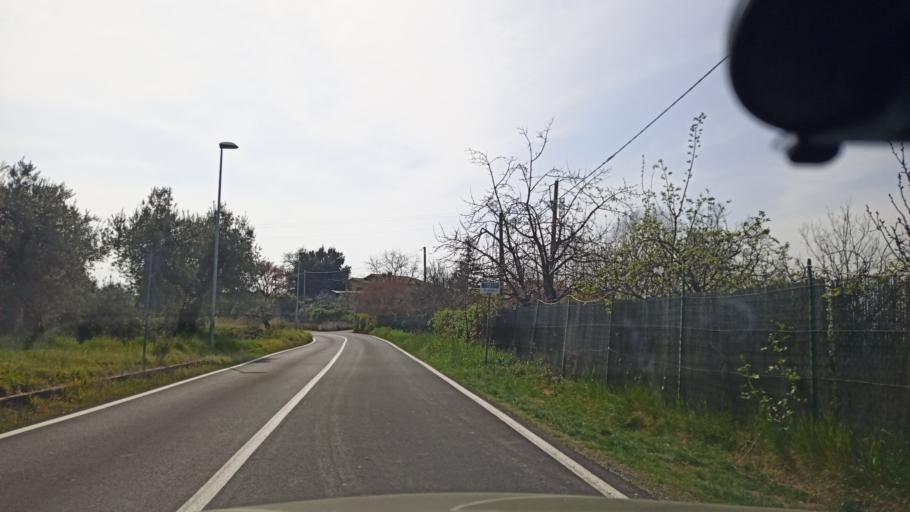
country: IT
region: Latium
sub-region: Provincia di Rieti
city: Torri in Sabina
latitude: 42.3407
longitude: 12.6511
